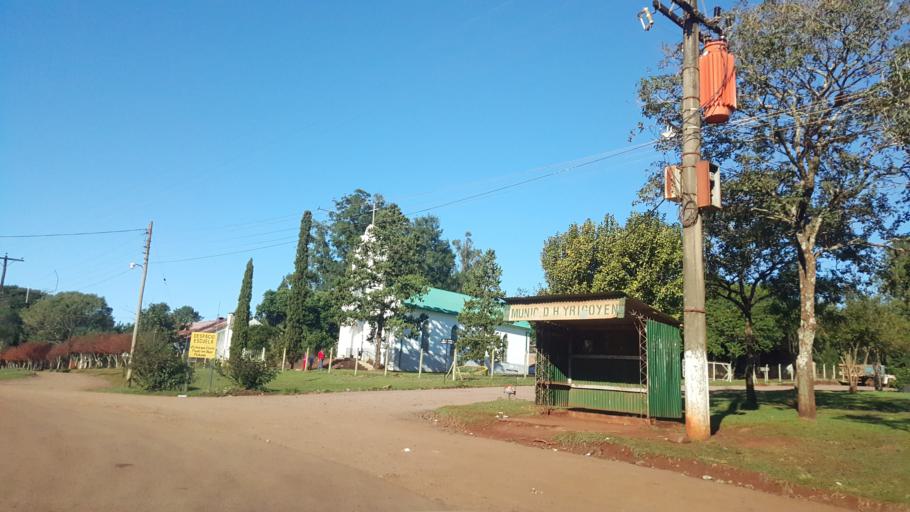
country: AR
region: Misiones
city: Jardin America
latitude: -27.0919
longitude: -55.2863
